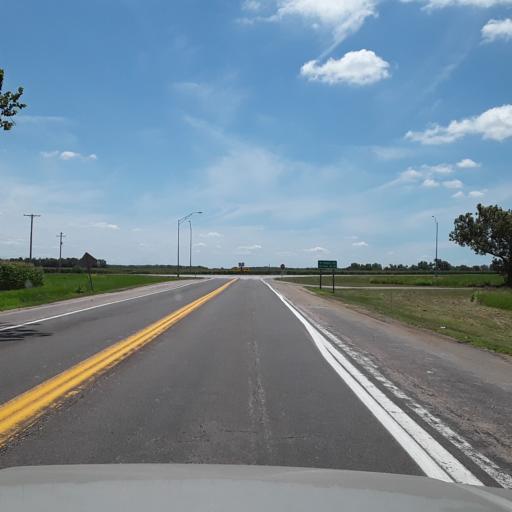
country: US
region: Nebraska
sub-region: Merrick County
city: Central City
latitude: 41.1926
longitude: -97.8723
